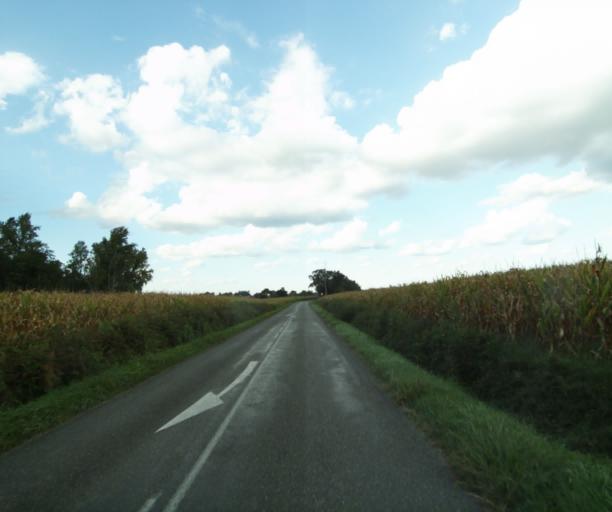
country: FR
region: Midi-Pyrenees
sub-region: Departement du Gers
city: Cazaubon
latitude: 43.9147
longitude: -0.0799
